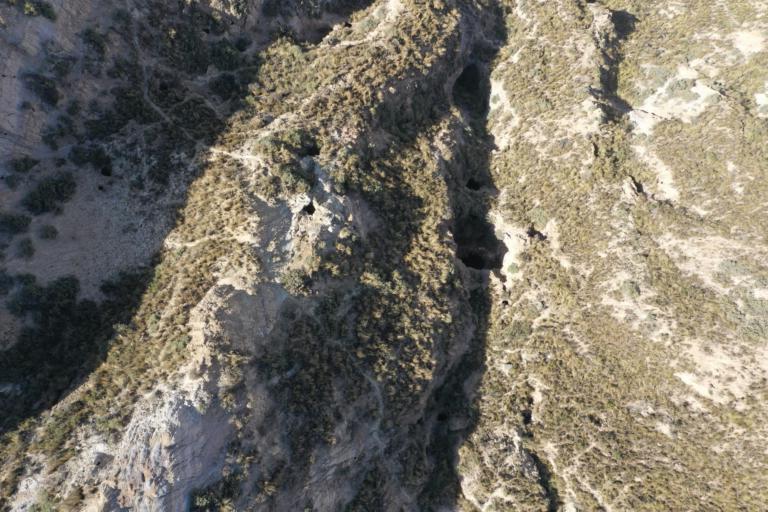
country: BO
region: La Paz
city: La Paz
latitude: -16.5518
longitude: -68.1295
